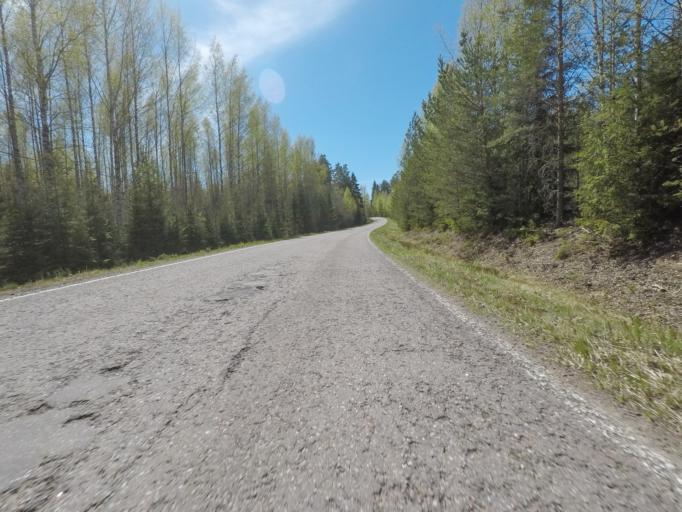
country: FI
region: Uusimaa
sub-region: Helsinki
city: Kaerkoelae
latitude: 60.5909
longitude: 23.7984
